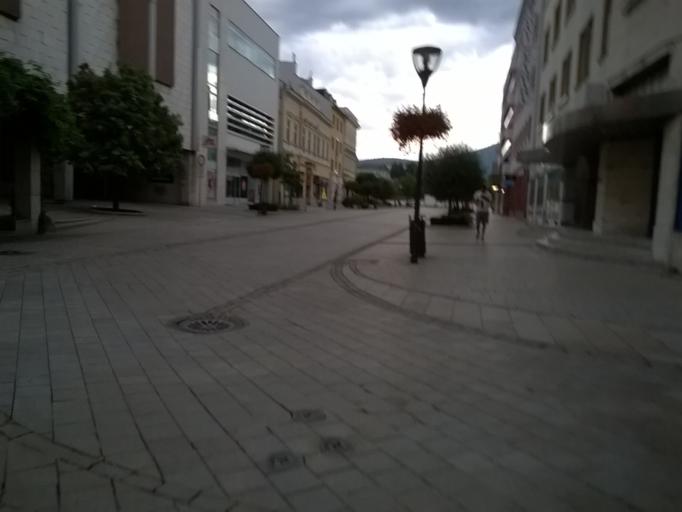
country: SK
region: Nitriansky
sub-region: Okres Nitra
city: Nitra
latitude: 48.3122
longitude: 18.0874
